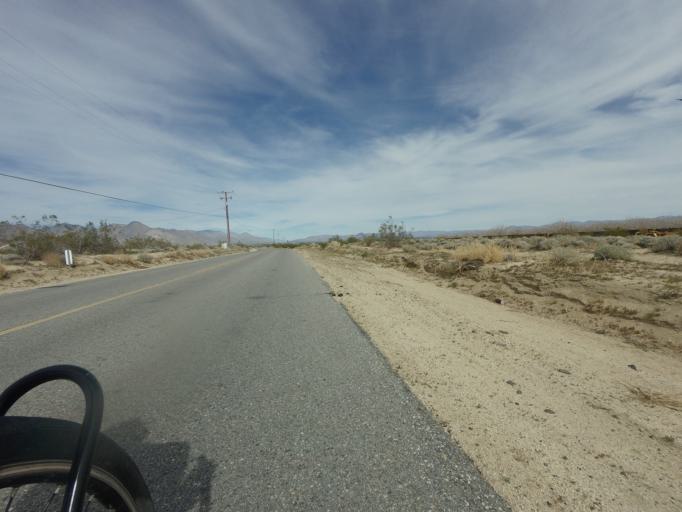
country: US
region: California
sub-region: Kern County
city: Inyokern
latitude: 35.7058
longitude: -117.8298
